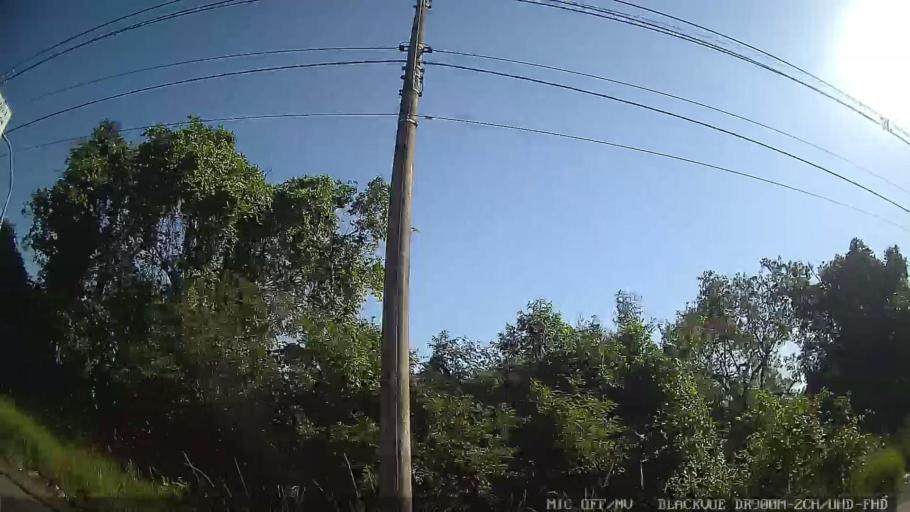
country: BR
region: Sao Paulo
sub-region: Santos
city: Santos
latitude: -23.9054
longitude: -46.3100
